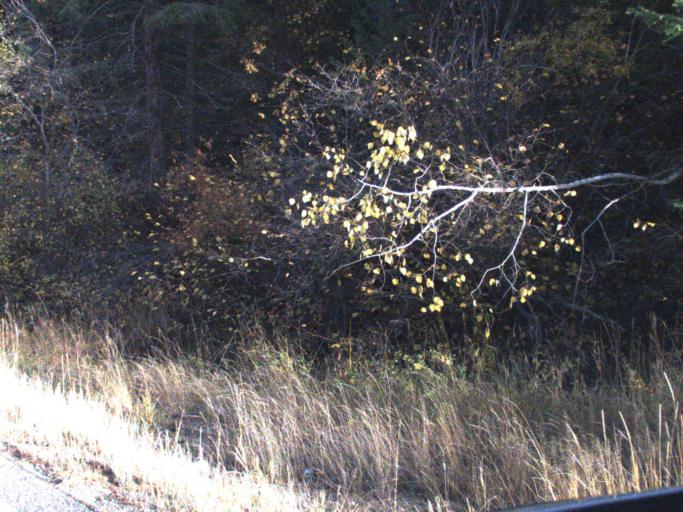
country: CA
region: British Columbia
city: Rossland
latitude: 48.8734
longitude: -117.8543
